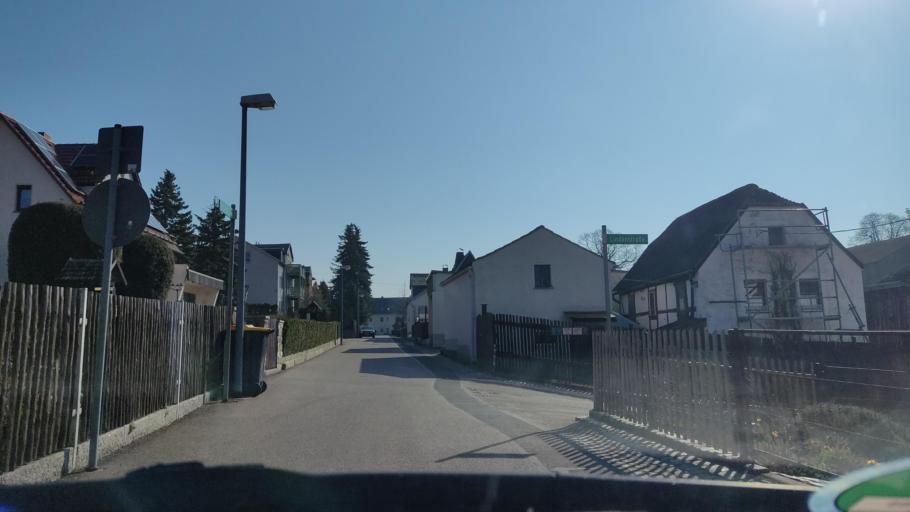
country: DE
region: Saxony
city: Tharandt
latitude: 51.0175
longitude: 13.5708
